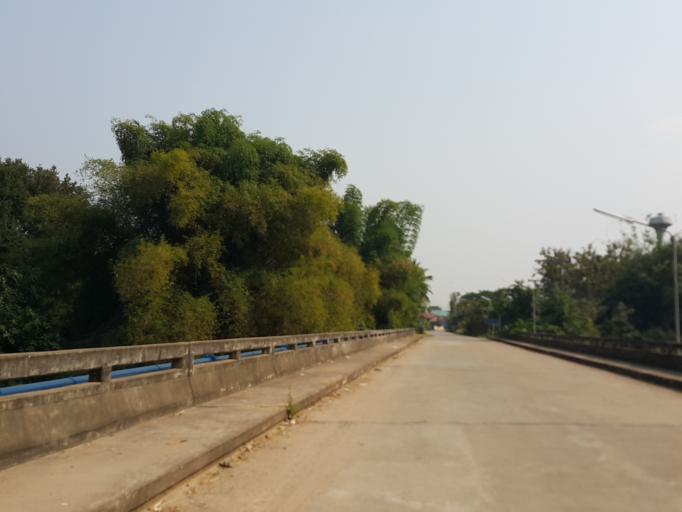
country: TH
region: Sukhothai
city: Thung Saliam
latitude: 17.3231
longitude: 99.5178
